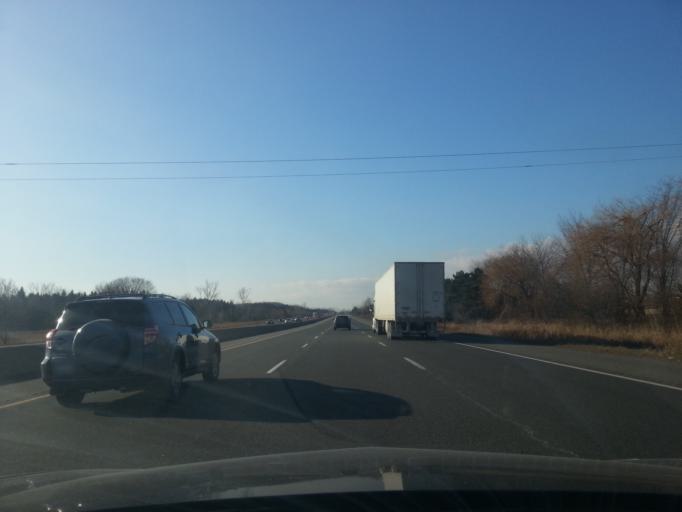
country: CA
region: Ontario
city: Oshawa
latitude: 43.8776
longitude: -78.7735
